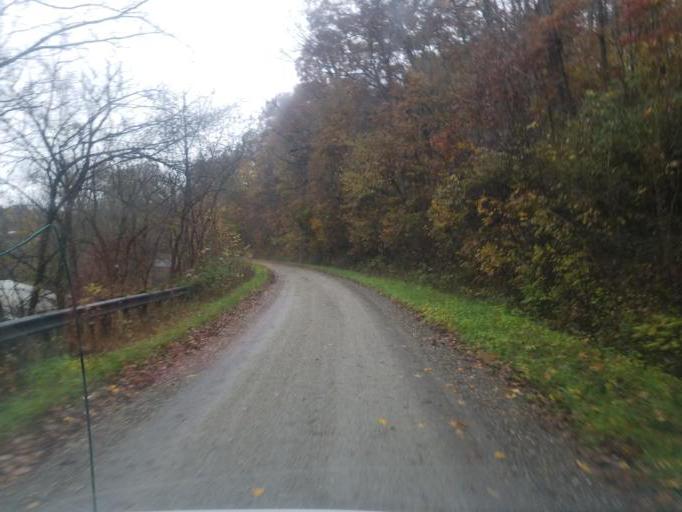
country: US
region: Ohio
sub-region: Washington County
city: Beverly
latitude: 39.4678
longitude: -81.7588
